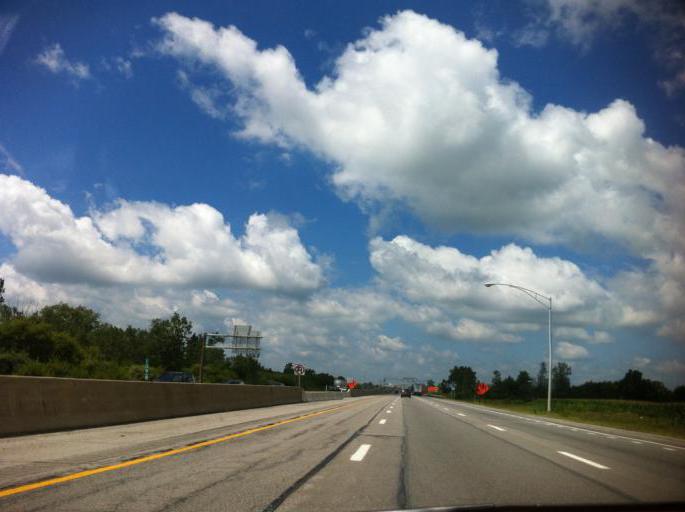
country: US
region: Ohio
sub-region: Huron County
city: Bellevue
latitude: 41.3423
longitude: -82.7737
